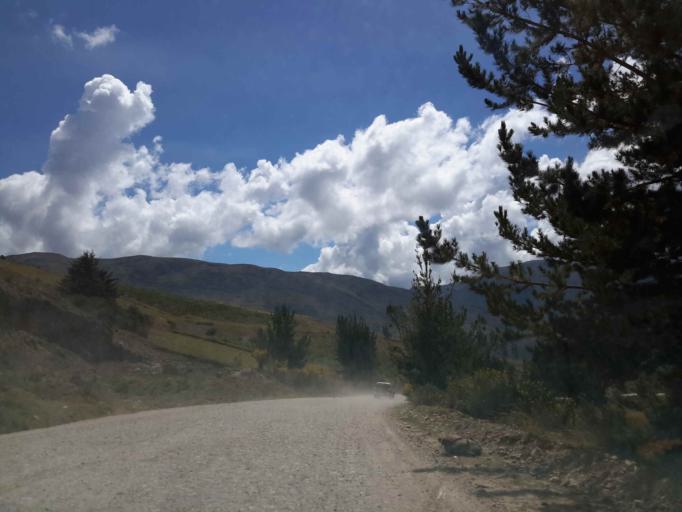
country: PE
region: Apurimac
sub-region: Provincia de Andahuaylas
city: Pacucha
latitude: -13.6242
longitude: -73.3383
